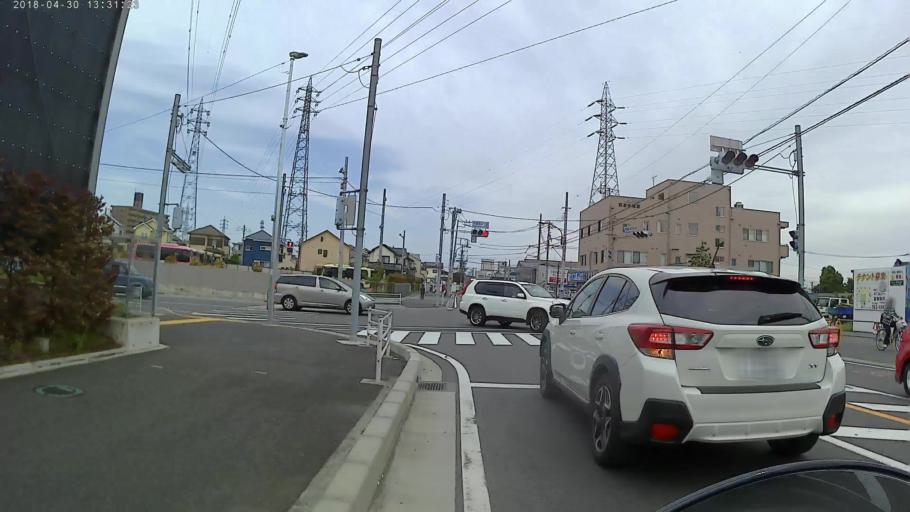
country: JP
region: Tokyo
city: Hachioji
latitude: 35.5916
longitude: 139.3273
